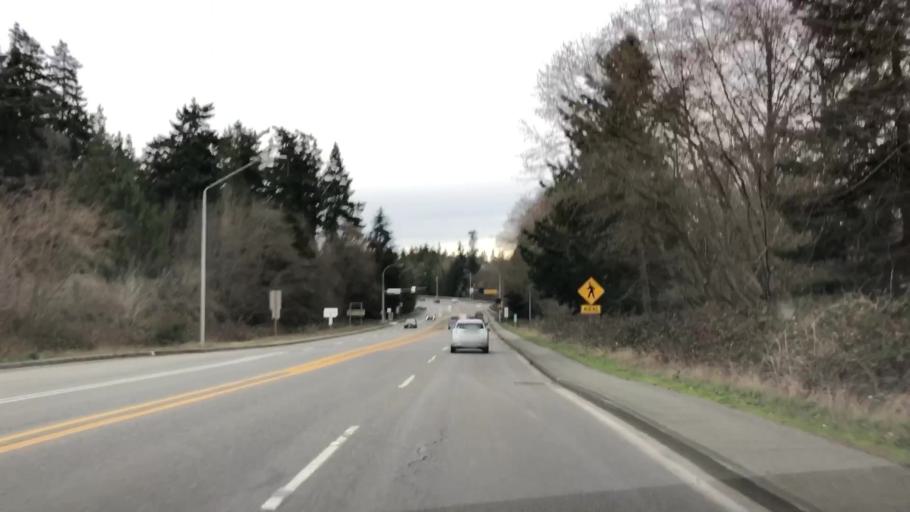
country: US
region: Washington
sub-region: Snohomish County
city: Edmonds
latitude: 47.8072
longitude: -122.3856
